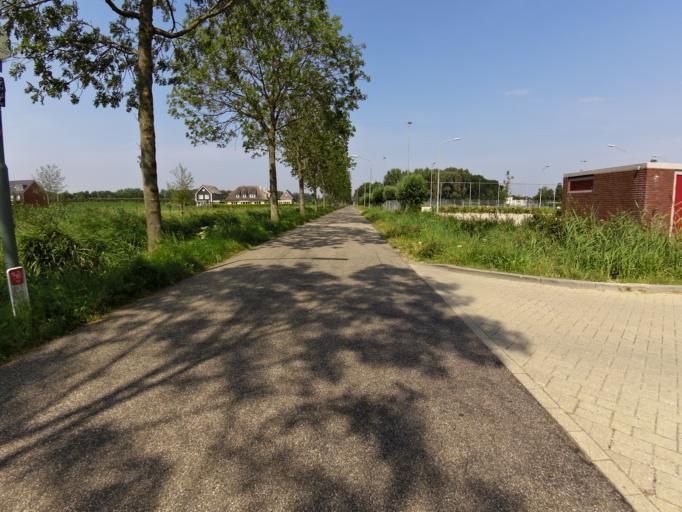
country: NL
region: South Holland
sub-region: Gemeente Dordrecht
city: Dordrecht
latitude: 51.7722
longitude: 4.6626
